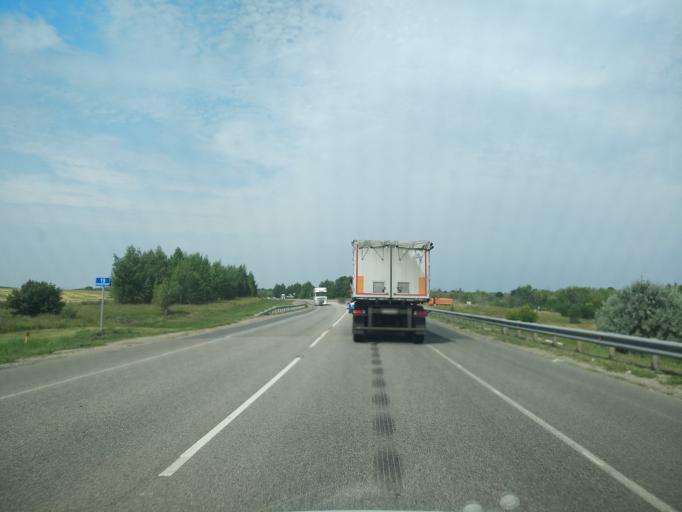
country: RU
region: Voronezj
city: Novaya Usman'
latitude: 51.7006
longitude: 39.4244
